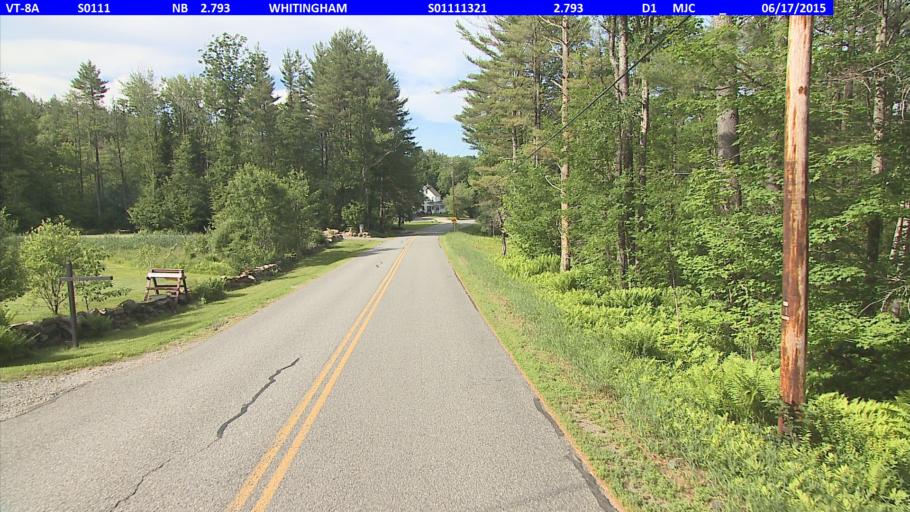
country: US
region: Massachusetts
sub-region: Franklin County
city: Colrain
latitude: 42.7725
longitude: -72.8077
